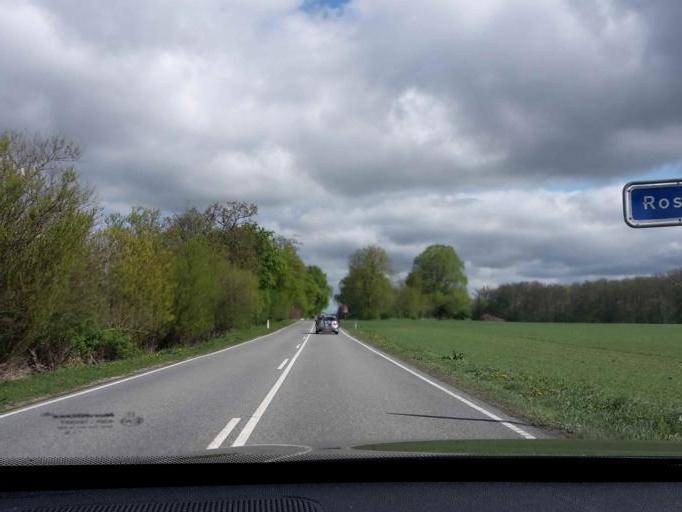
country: DK
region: Central Jutland
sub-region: Syddjurs Kommune
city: Hornslet
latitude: 56.3288
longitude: 10.3298
